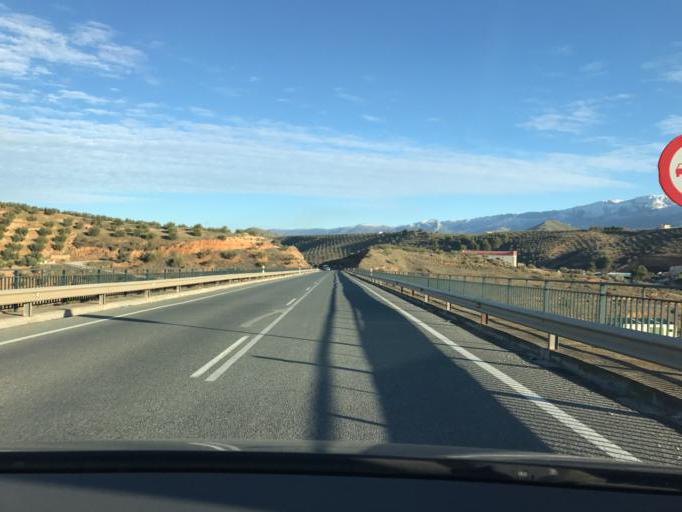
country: ES
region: Andalusia
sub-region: Provincia de Granada
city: Iznalloz
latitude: 37.4018
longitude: -3.5285
